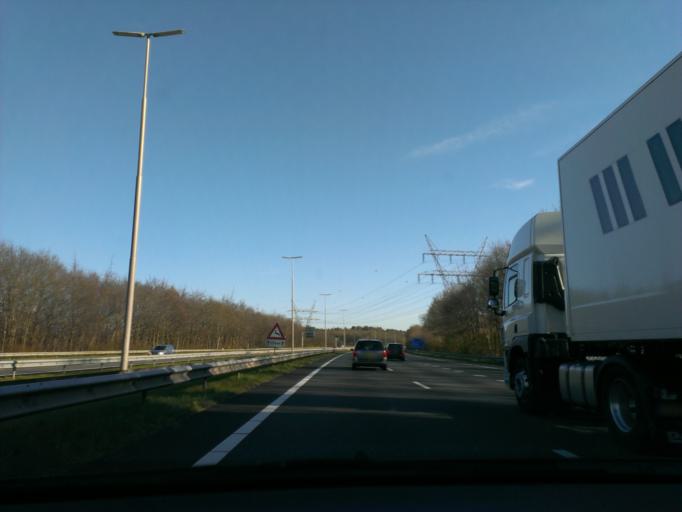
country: NL
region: Gelderland
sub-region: Gemeente Hattem
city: Hattem
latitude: 52.4762
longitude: 6.0354
